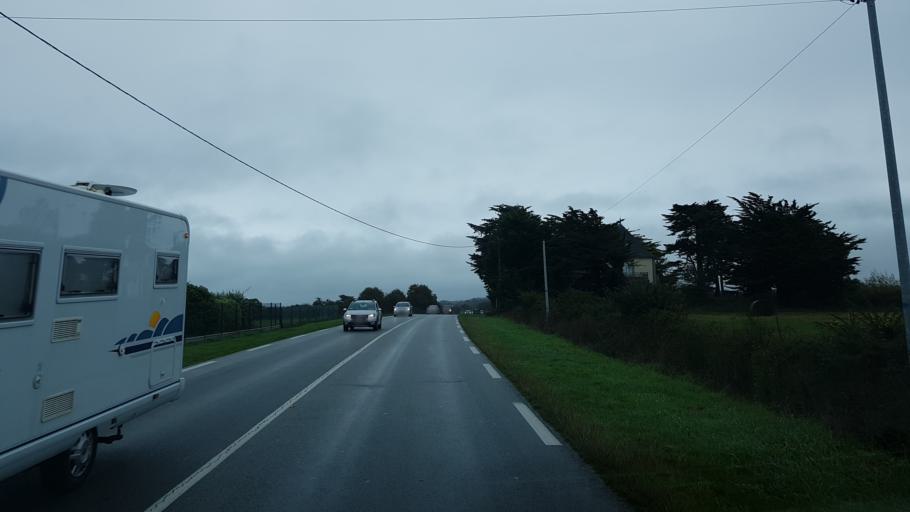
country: FR
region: Brittany
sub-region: Departement du Morbihan
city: Saint-Gildas-de-Rhuys
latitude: 47.5318
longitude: -2.8388
